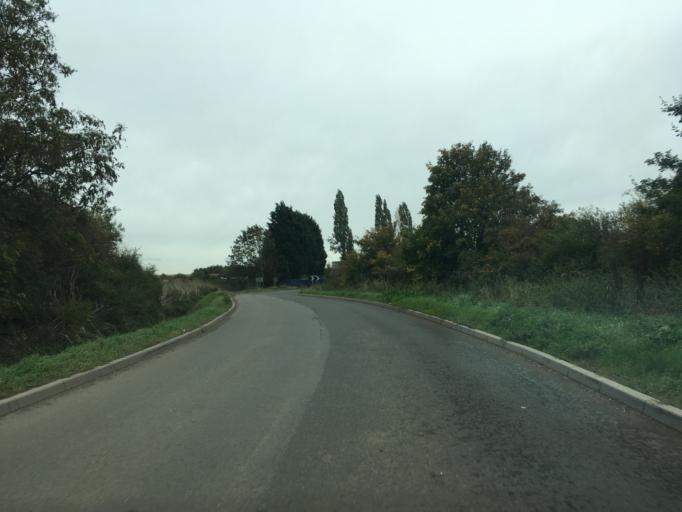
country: GB
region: England
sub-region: Nottinghamshire
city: Newark on Trent
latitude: 53.0488
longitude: -0.8043
